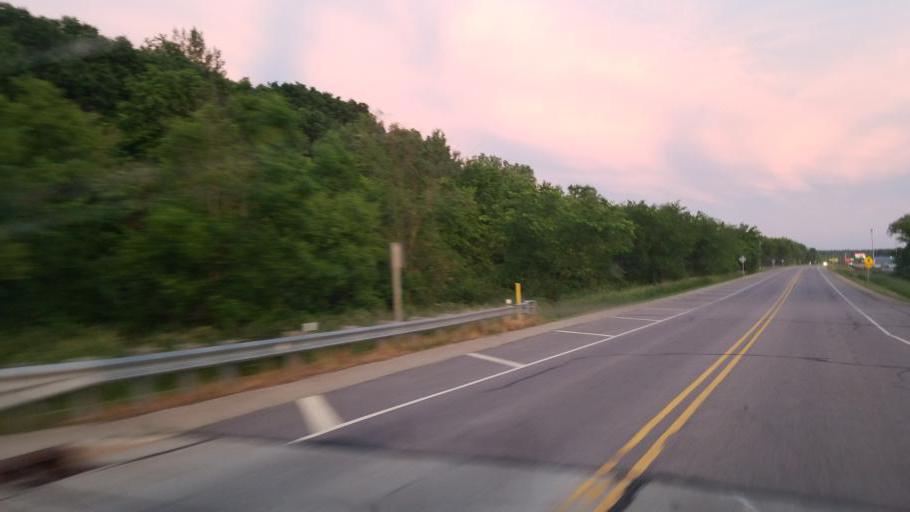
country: US
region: Wisconsin
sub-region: Juneau County
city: Elroy
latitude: 43.7335
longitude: -90.2677
